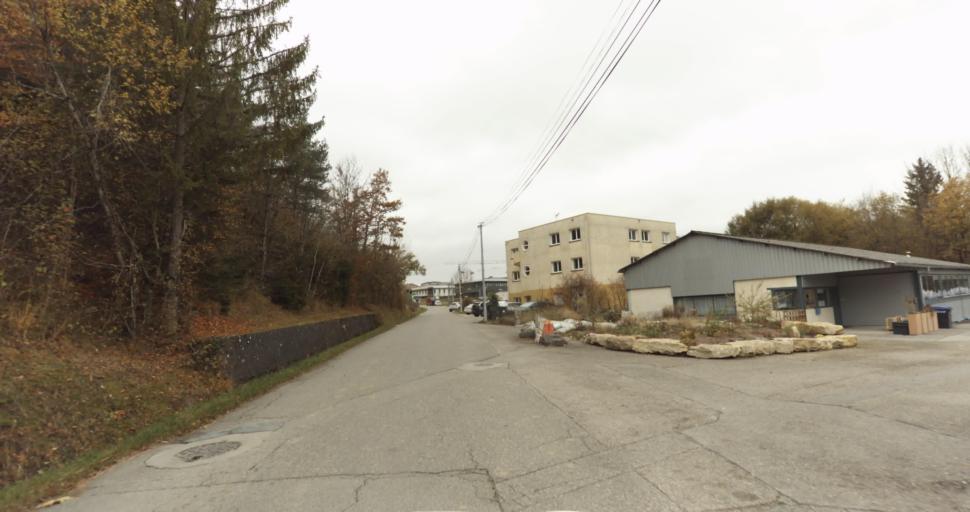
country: FR
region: Rhone-Alpes
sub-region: Departement de la Haute-Savoie
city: Chavanod
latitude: 45.8838
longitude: 6.0611
